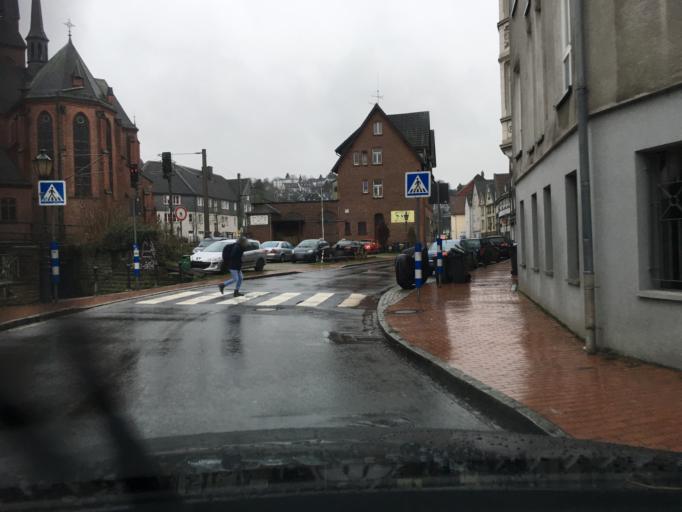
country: DE
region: North Rhine-Westphalia
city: Hattingen
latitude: 51.3543
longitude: 7.1217
